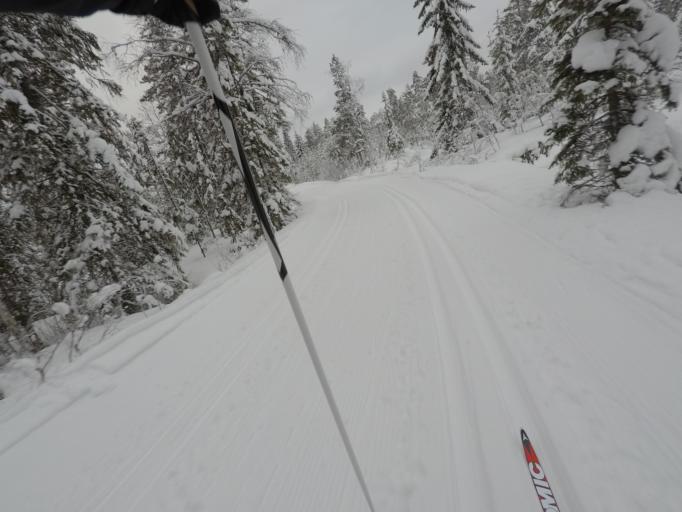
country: SE
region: Dalarna
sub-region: Ludvika Kommun
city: Abborrberget
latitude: 60.1625
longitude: 14.4804
